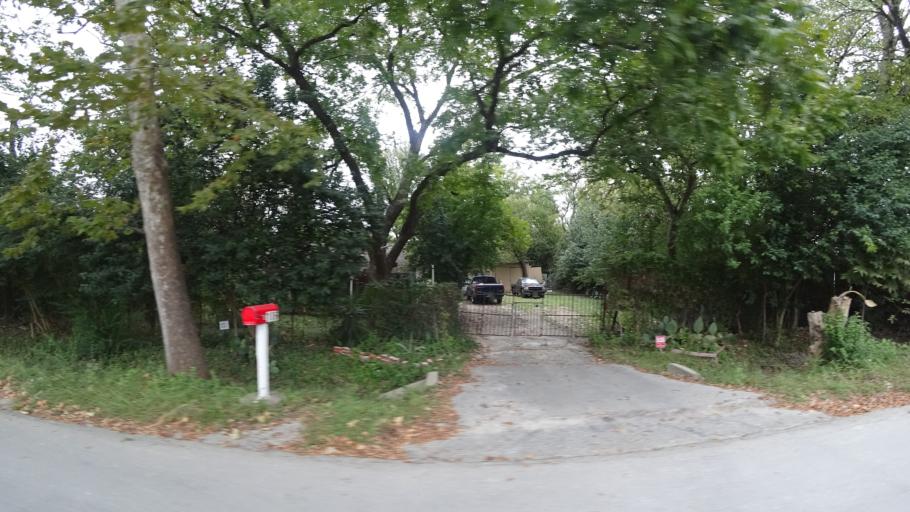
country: US
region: Texas
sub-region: Travis County
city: Austin
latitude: 30.2067
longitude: -97.7752
